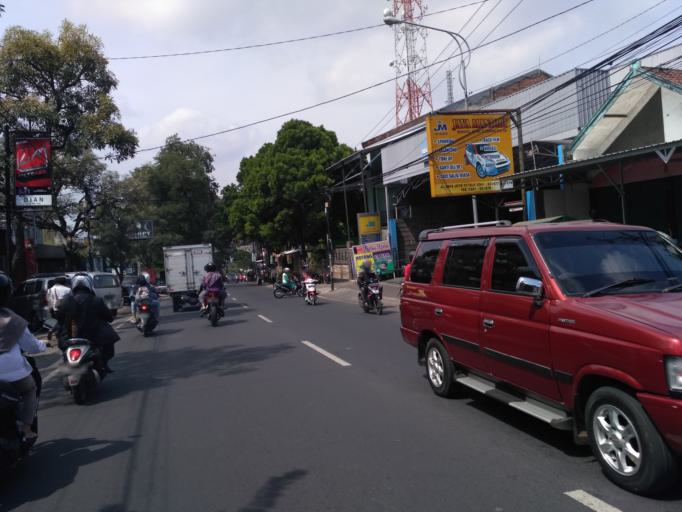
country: ID
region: East Java
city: Malang
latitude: -7.9196
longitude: 112.5931
